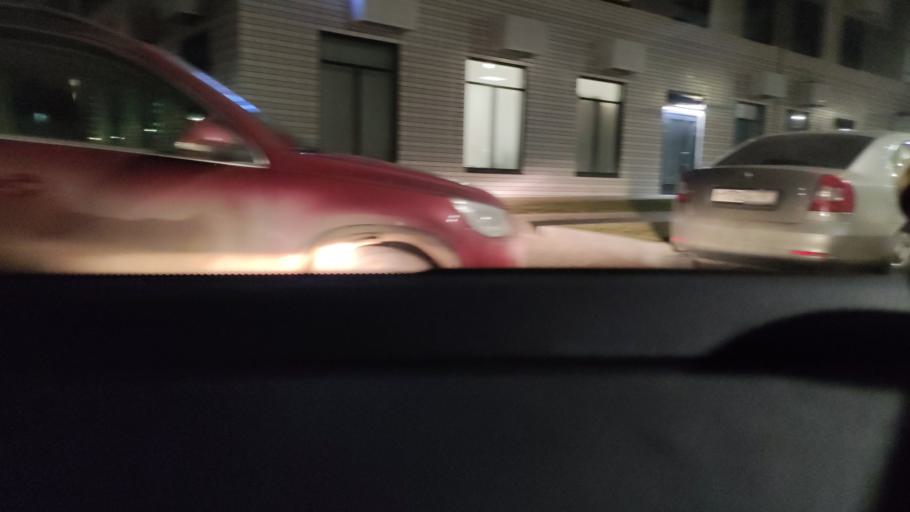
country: RU
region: Moscow
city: Bibirevo
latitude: 55.8765
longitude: 37.6032
